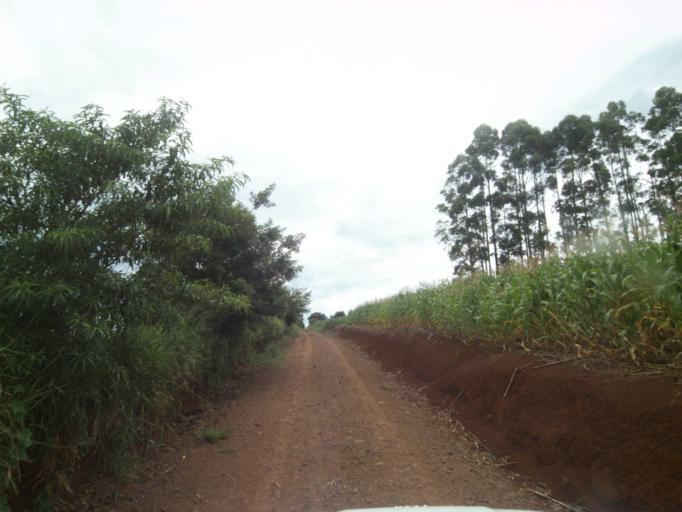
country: BR
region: Parana
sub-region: Guaraniacu
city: Guaraniacu
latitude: -24.9135
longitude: -52.9353
